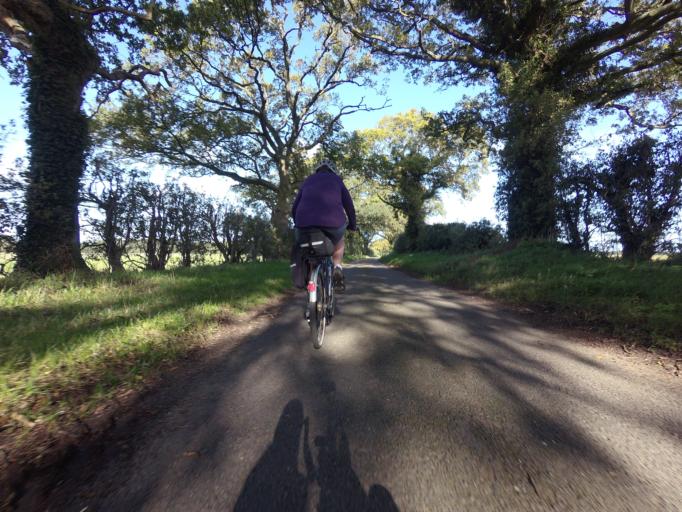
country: GB
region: England
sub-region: Norfolk
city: Fakenham
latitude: 52.8424
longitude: 0.6825
